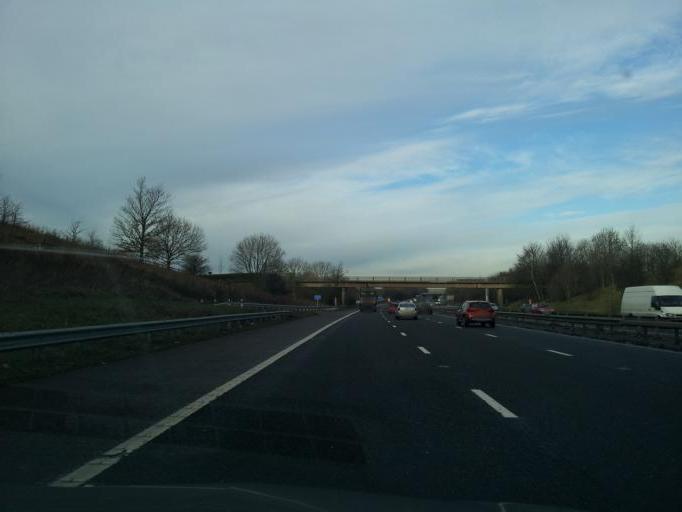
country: GB
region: England
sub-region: Borough of Bury
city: Prestwich
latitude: 53.5566
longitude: -2.2669
